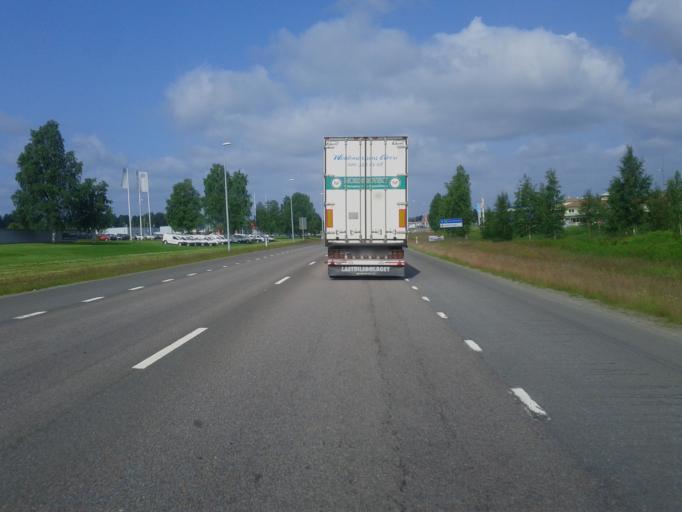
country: SE
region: Vaesterbotten
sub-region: Skelleftea Kommun
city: Skelleftea
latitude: 64.7331
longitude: 20.9710
